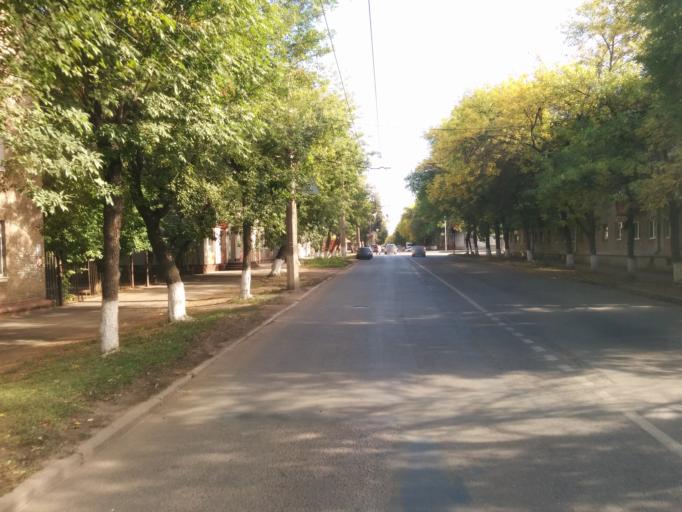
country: RU
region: Bashkortostan
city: Ufa
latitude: 54.8234
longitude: 56.0659
